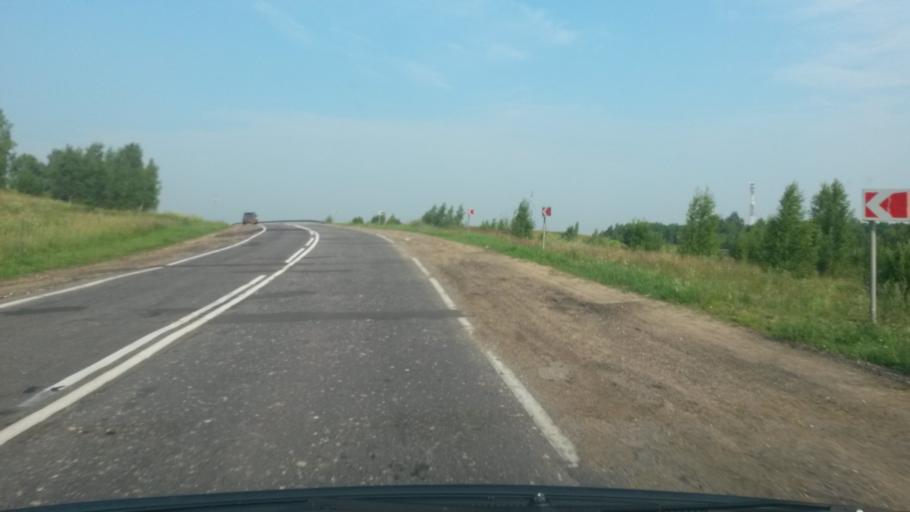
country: RU
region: Jaroslavl
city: Gavrilov-Yam
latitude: 57.3593
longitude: 39.7795
